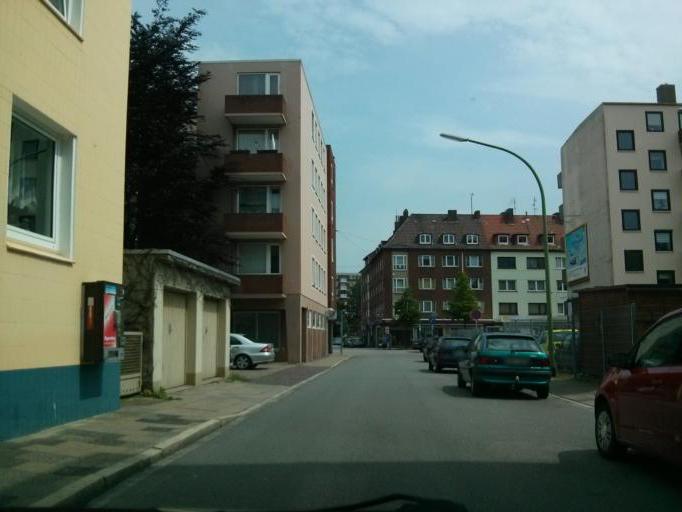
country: DE
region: Bremen
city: Bremerhaven
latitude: 53.5332
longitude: 8.5881
